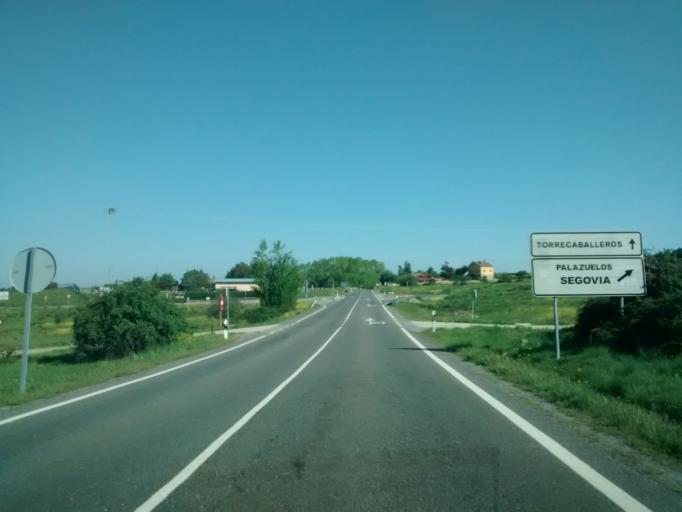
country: ES
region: Castille and Leon
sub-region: Provincia de Segovia
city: Palazuelos de Eresma
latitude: 40.9267
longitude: -4.0295
